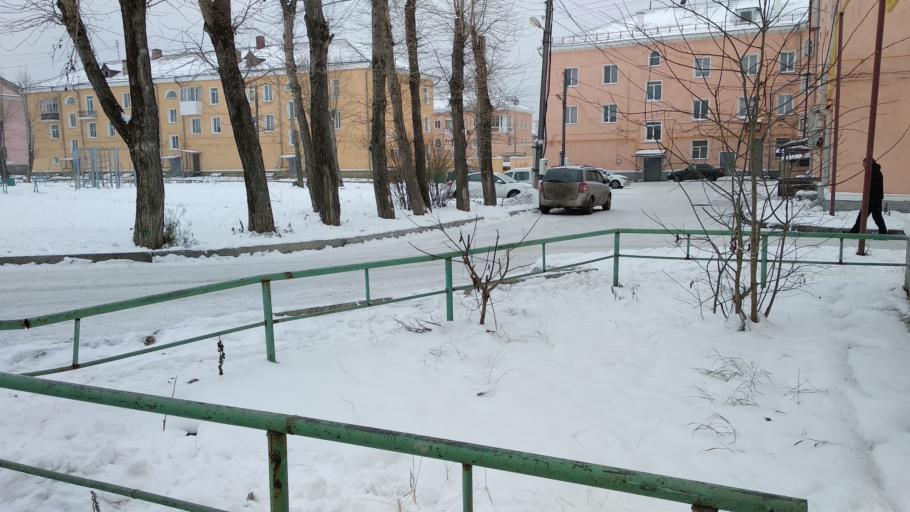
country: RU
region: Sverdlovsk
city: Krasnotur'insk
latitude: 59.7646
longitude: 60.1877
